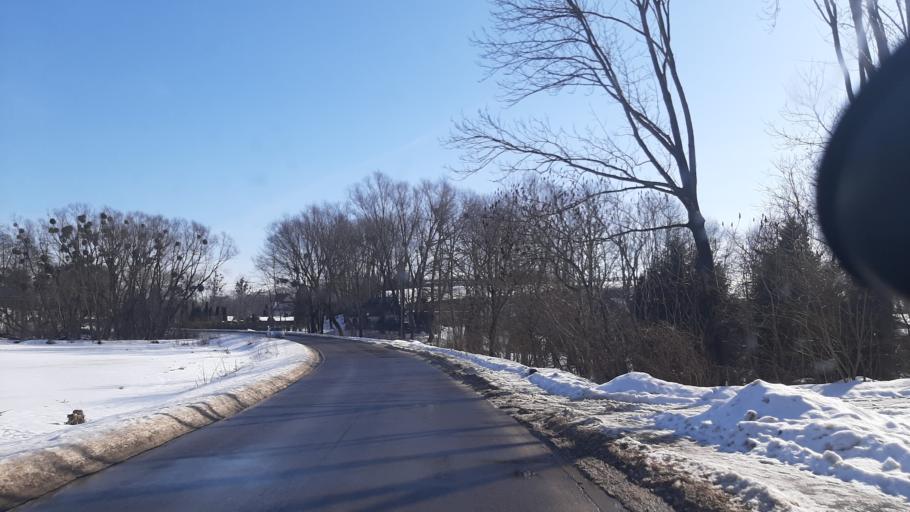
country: PL
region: Lublin Voivodeship
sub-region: Powiat pulawski
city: Wawolnica
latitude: 51.3562
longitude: 22.1237
